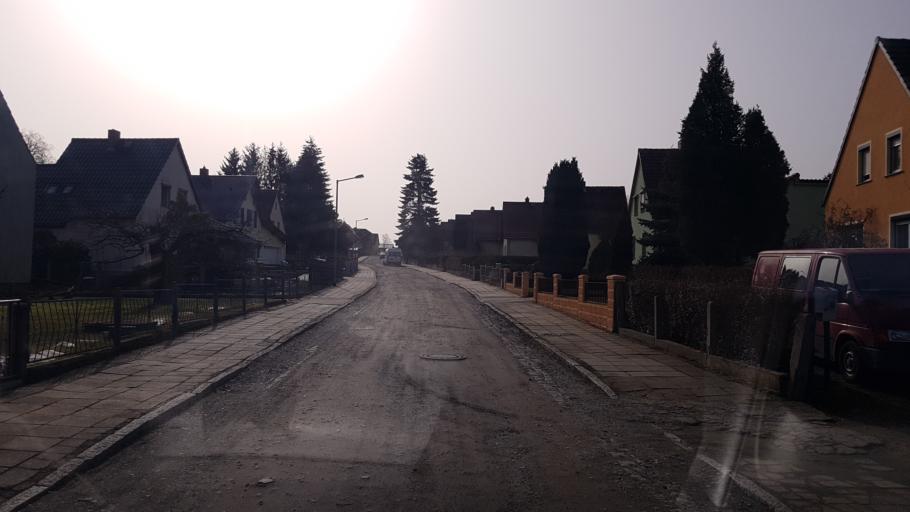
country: DE
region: Brandenburg
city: Lauchhammer
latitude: 51.5076
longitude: 13.7922
